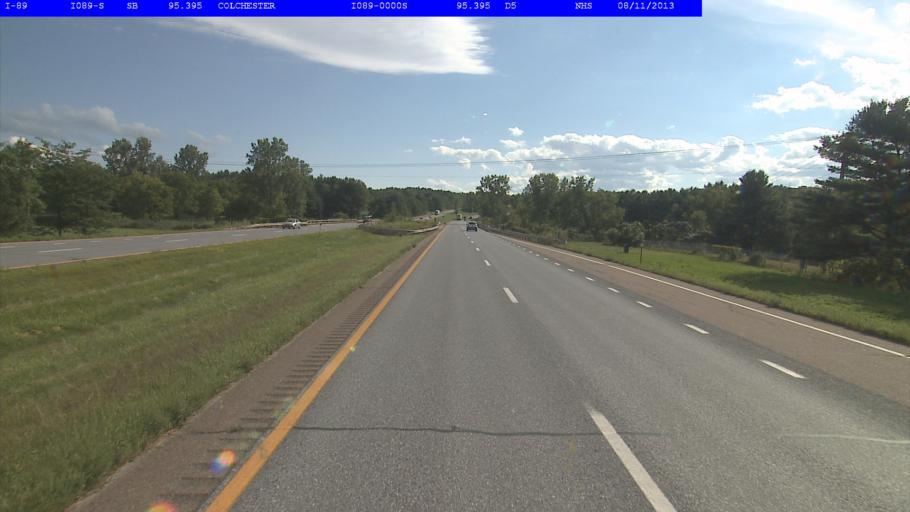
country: US
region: Vermont
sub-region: Chittenden County
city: Colchester
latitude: 44.5556
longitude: -73.1840
